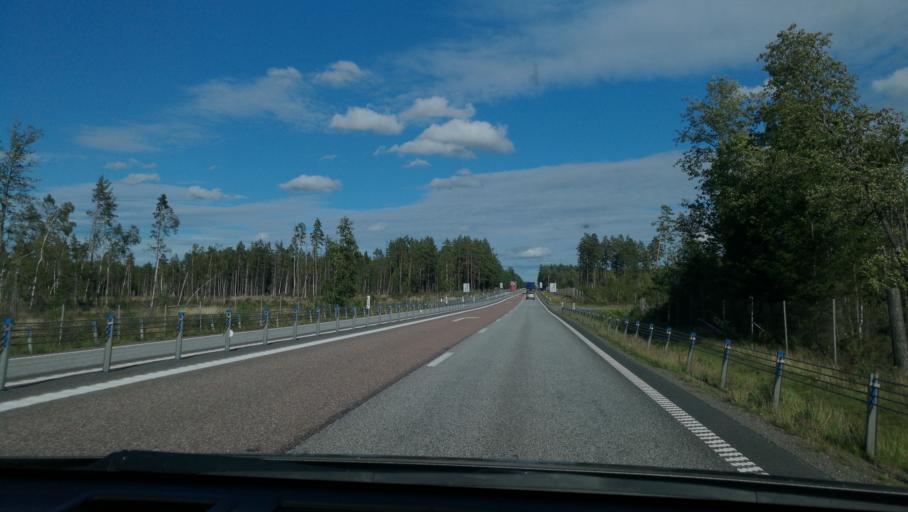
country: SE
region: OErebro
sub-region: Laxa Kommun
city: Laxa
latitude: 58.9932
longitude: 14.6638
